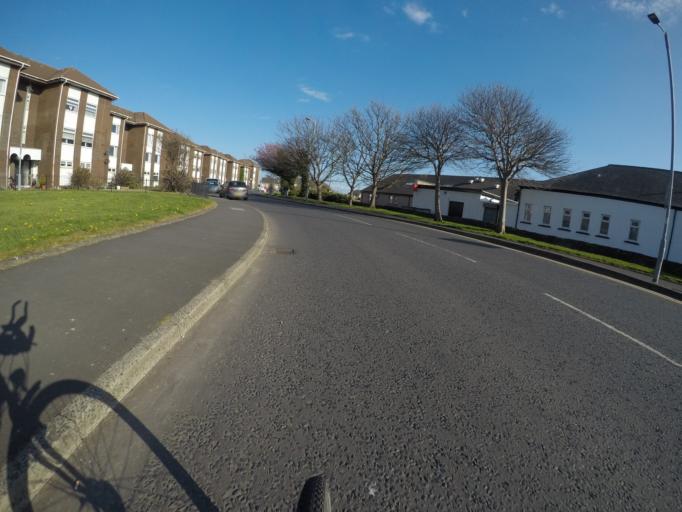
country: GB
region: Scotland
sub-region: North Ayrshire
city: Saltcoats
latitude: 55.6352
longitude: -4.7836
